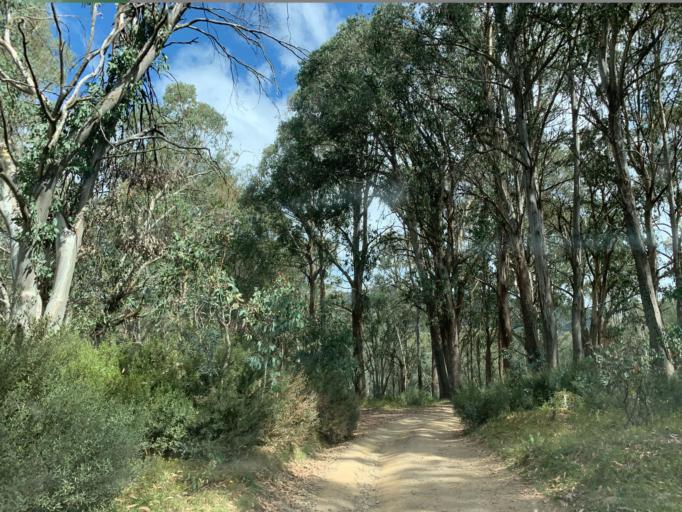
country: AU
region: Victoria
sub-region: Mansfield
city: Mansfield
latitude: -37.1040
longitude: 146.5378
